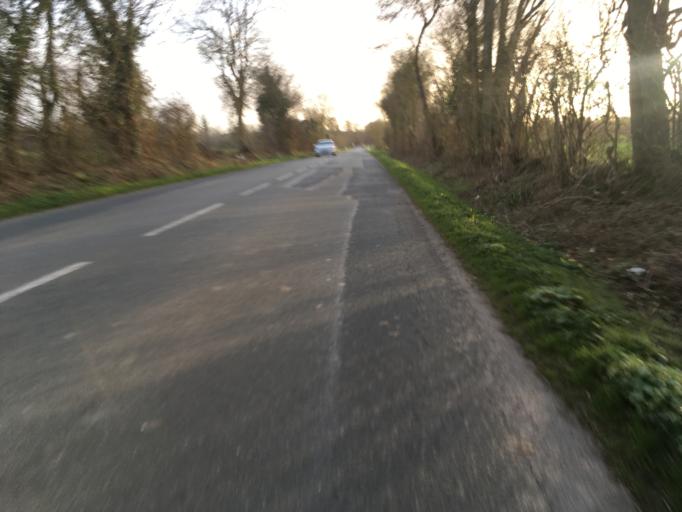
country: FR
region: Poitou-Charentes
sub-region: Departement de la Charente-Maritime
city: Courcon
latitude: 46.1720
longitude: -0.8482
